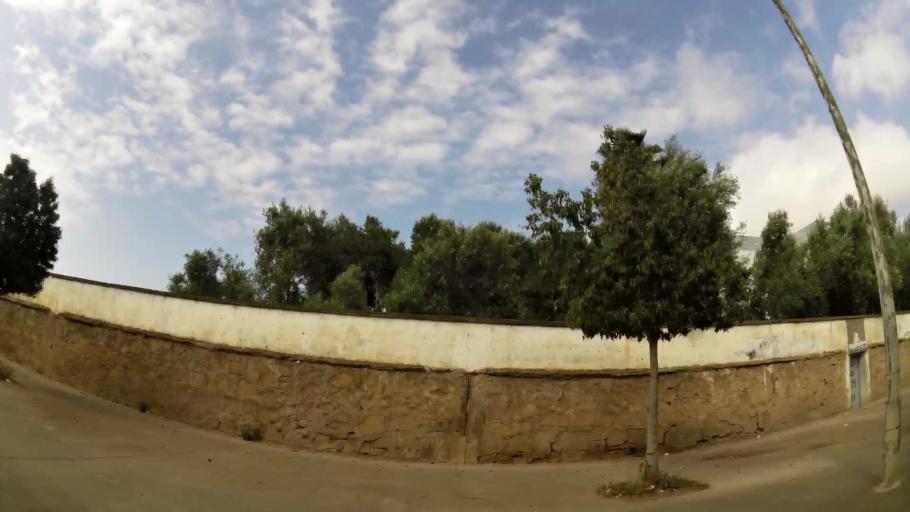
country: MA
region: Rabat-Sale-Zemmour-Zaer
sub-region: Khemisset
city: Tiflet
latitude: 33.8866
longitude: -6.3158
